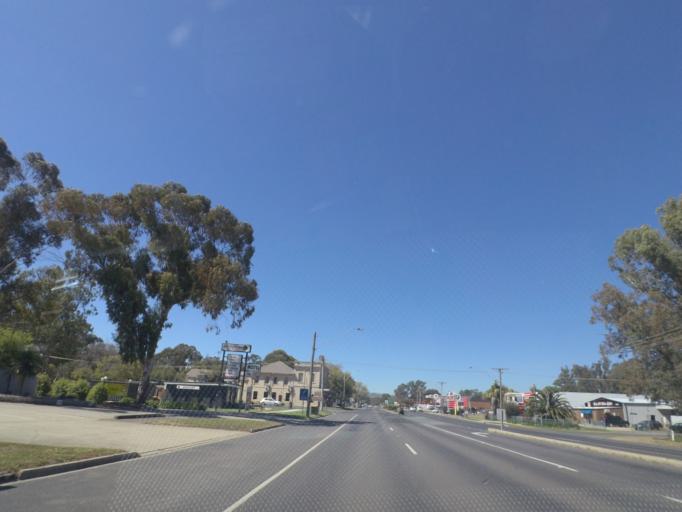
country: AU
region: Victoria
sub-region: Murrindindi
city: Kinglake West
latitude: -37.0208
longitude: 145.1260
